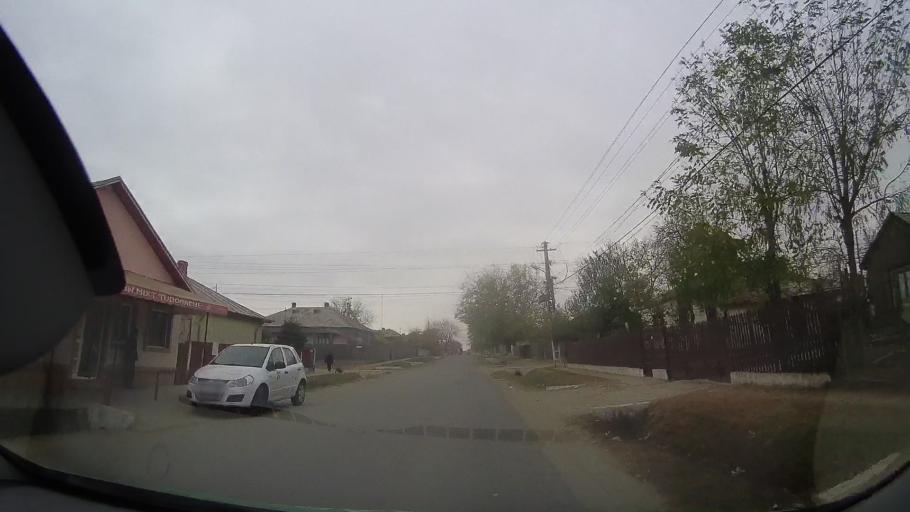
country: RO
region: Buzau
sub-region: Comuna Rusetu
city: Rusetu
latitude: 44.9636
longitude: 27.2118
